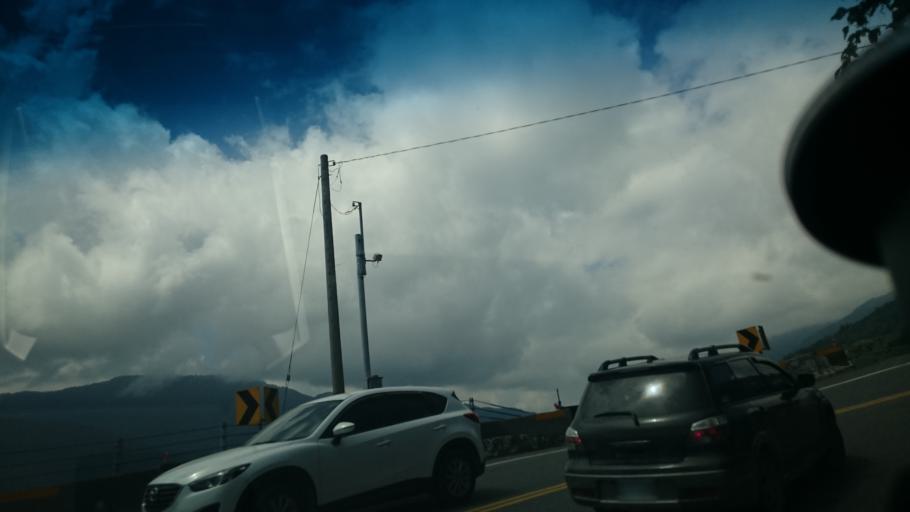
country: TW
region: Taiwan
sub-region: Nantou
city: Puli
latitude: 24.0394
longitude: 121.1450
